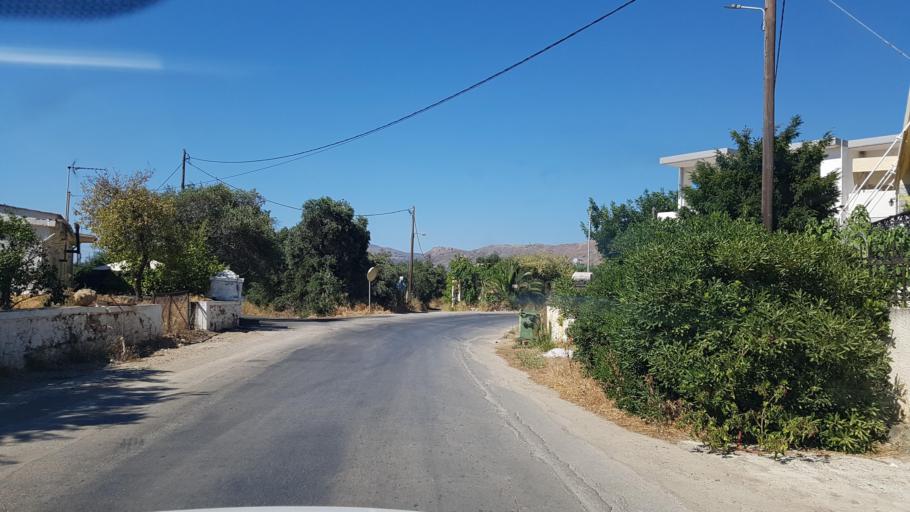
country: GR
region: Crete
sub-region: Nomos Chanias
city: Kissamos
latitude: 35.4935
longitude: 23.7050
